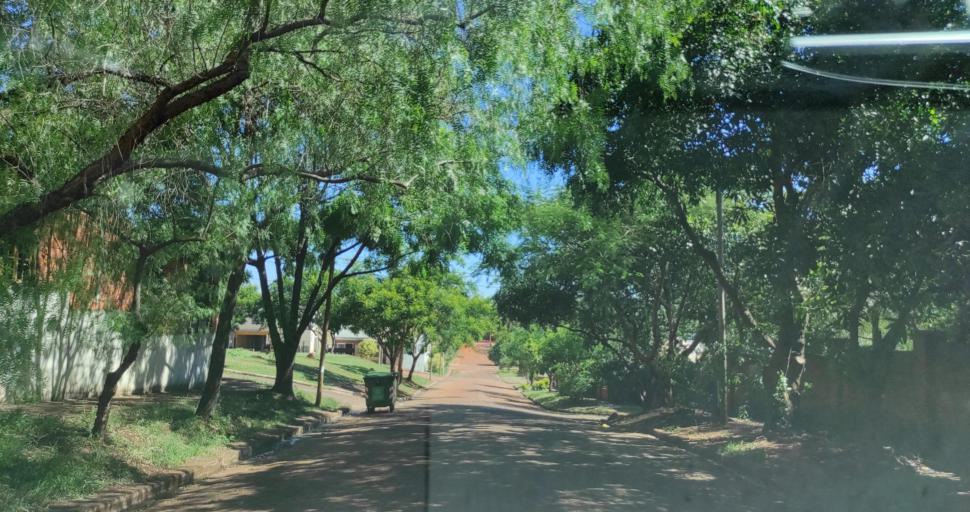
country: AR
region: Misiones
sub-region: Departamento de Capital
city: Posadas
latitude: -27.3975
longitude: -55.9455
